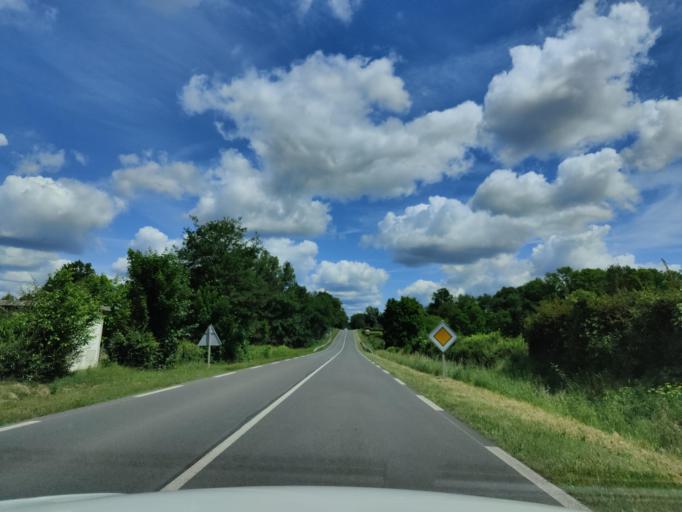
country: FR
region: Auvergne
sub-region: Departement de l'Allier
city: Vallon-en-Sully
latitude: 46.4916
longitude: 2.6191
